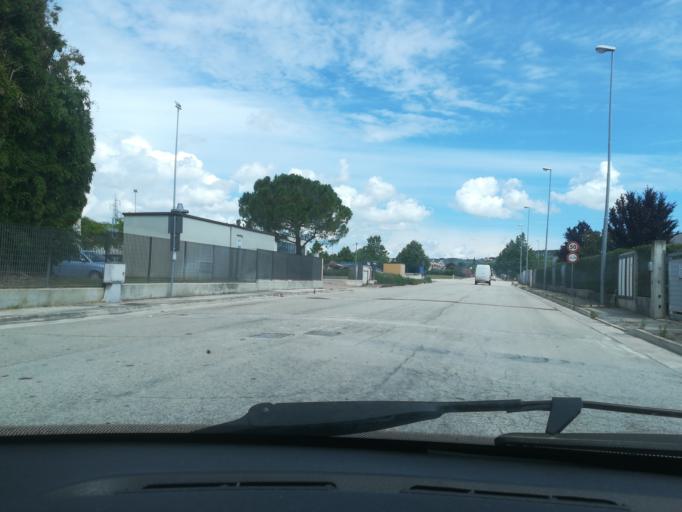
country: IT
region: The Marches
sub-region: Provincia di Macerata
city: Santa Maria Apparente
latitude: 43.2823
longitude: 13.6761
